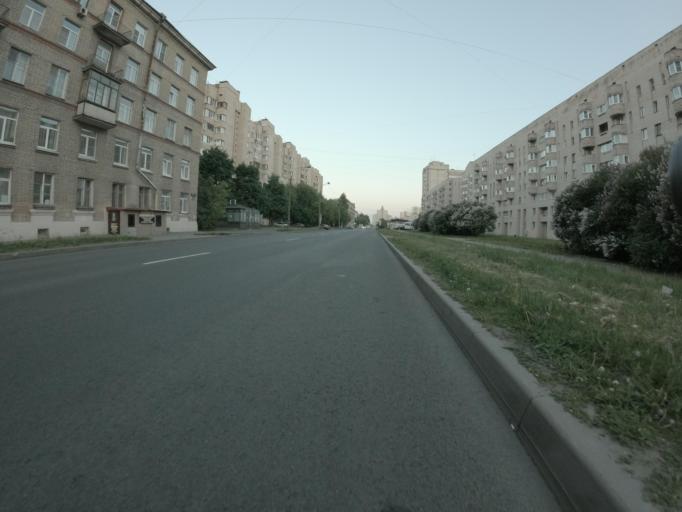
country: RU
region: St.-Petersburg
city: Kupchino
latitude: 59.8502
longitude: 30.3148
